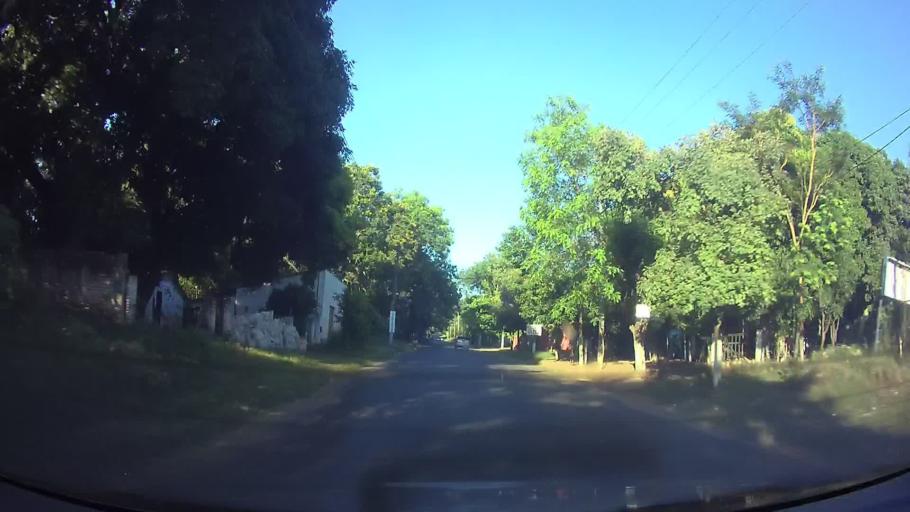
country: PY
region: Cordillera
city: San Bernardino
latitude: -25.3208
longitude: -57.2734
